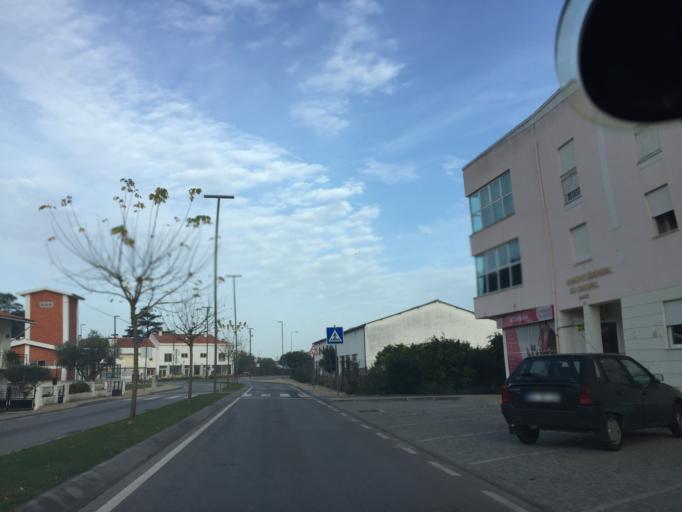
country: PT
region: Aveiro
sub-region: Anadia
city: Arcos
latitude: 40.4461
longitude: -8.4365
